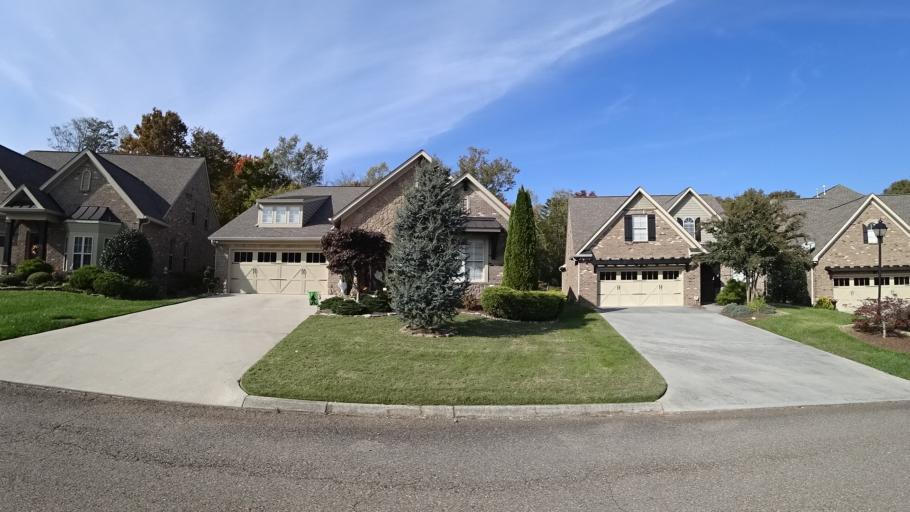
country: US
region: Tennessee
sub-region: Knox County
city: Farragut
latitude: 35.9238
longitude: -84.1563
